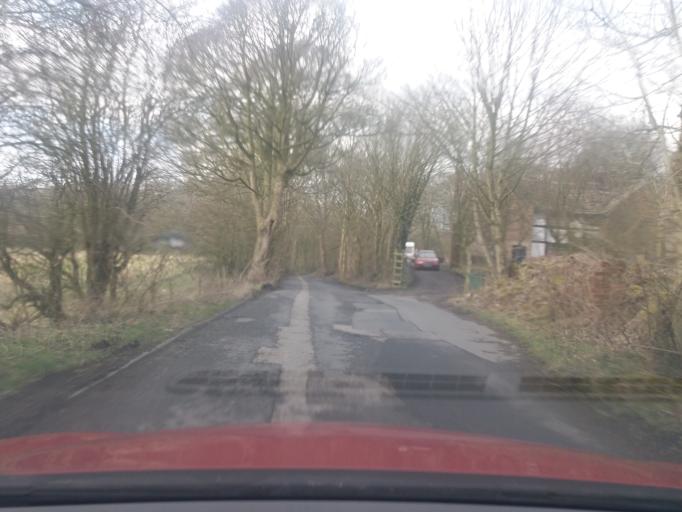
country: GB
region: England
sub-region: Lancashire
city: Coppull
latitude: 53.6355
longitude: -2.6497
